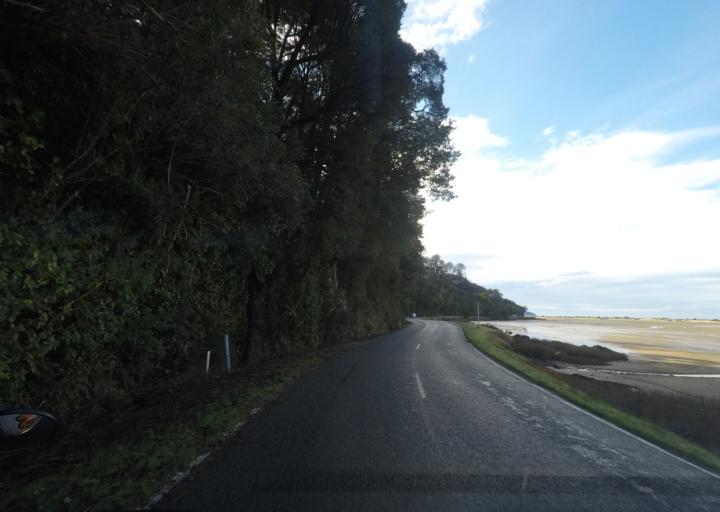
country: NZ
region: Tasman
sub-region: Tasman District
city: Motueka
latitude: -41.0134
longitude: 172.9980
